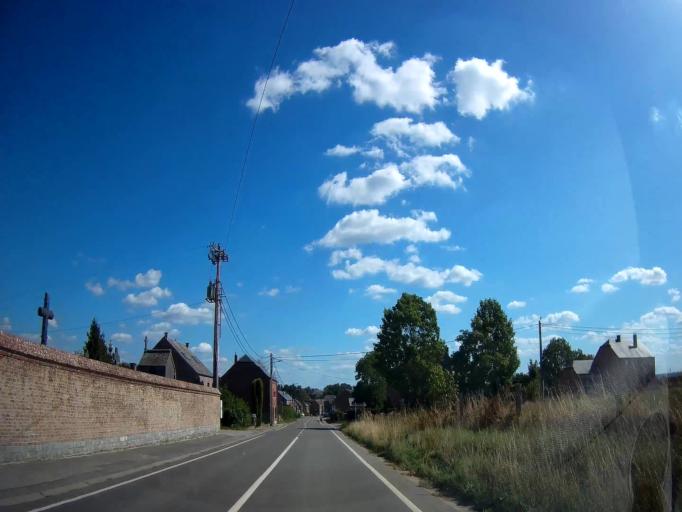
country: FR
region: Champagne-Ardenne
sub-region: Departement des Ardennes
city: Fromelennes
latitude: 50.1706
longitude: 4.8800
